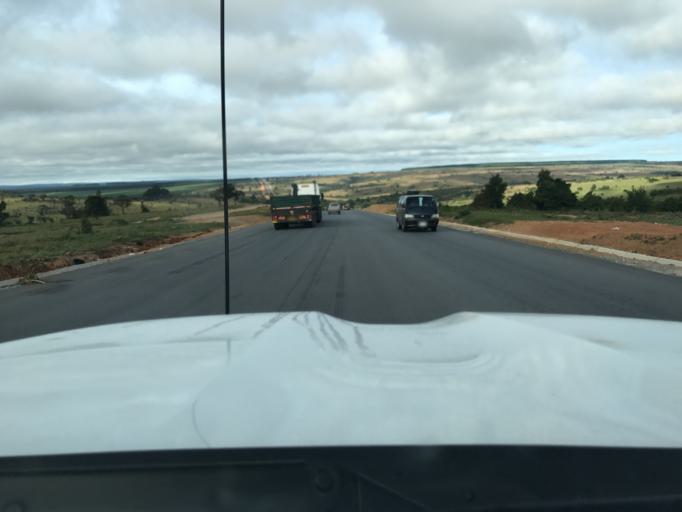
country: TZ
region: Iringa
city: Makungu
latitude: -8.3359
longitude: 35.2547
